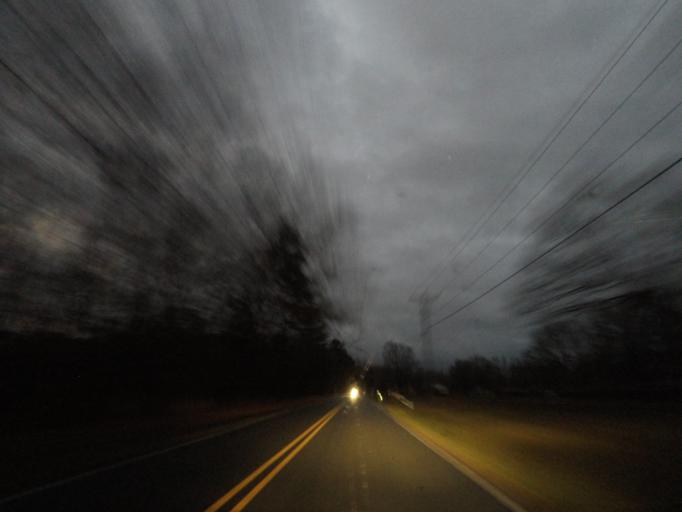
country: US
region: North Carolina
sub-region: Orange County
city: Hillsborough
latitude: 36.0657
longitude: -78.9974
